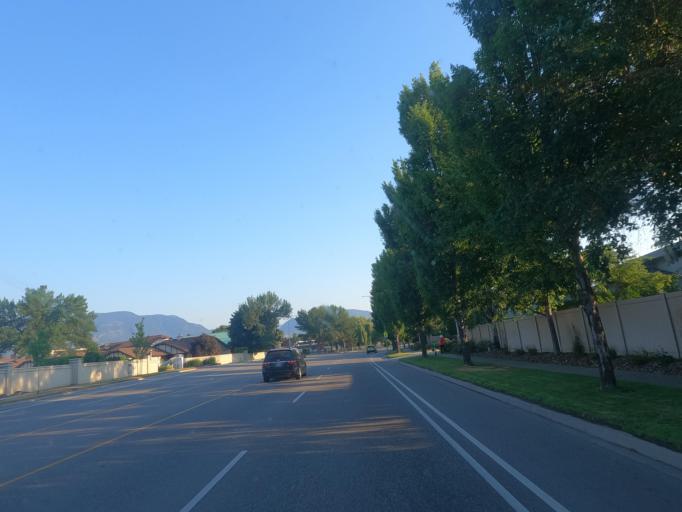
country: CA
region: British Columbia
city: Kelowna
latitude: 49.8739
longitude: -119.4765
